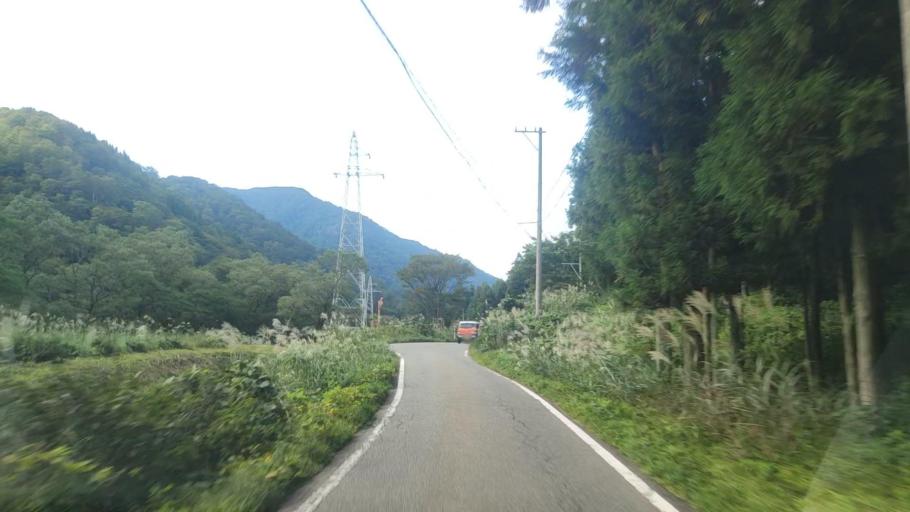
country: JP
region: Toyama
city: Yatsuomachi-higashikumisaka
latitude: 36.4450
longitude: 137.0841
